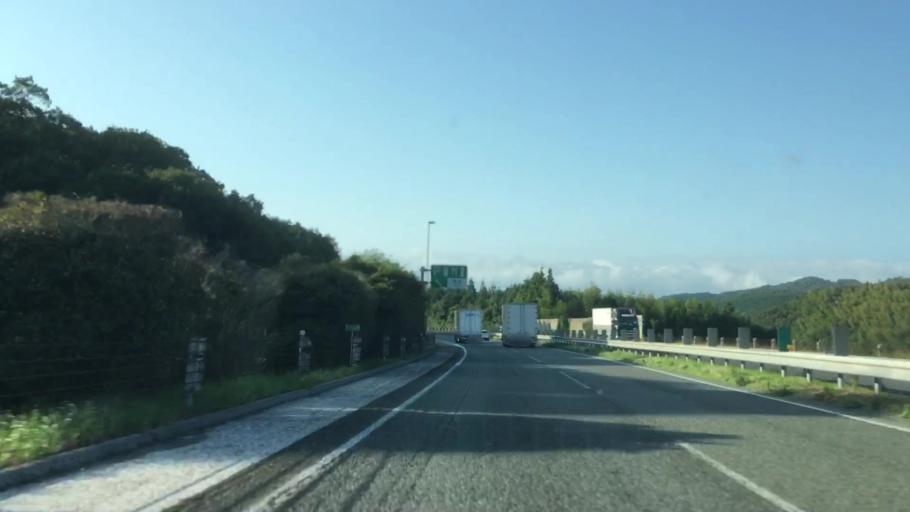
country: JP
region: Yamaguchi
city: Ogori-shimogo
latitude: 34.1501
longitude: 131.3422
